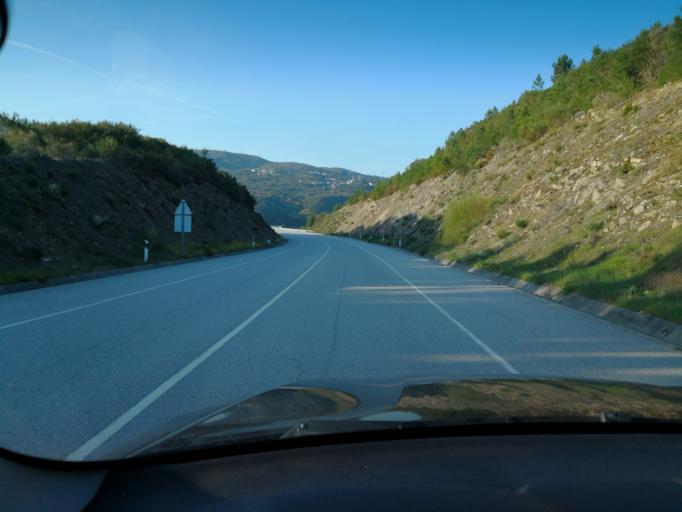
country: PT
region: Vila Real
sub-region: Vila Real
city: Vila Real
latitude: 41.3622
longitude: -7.7081
